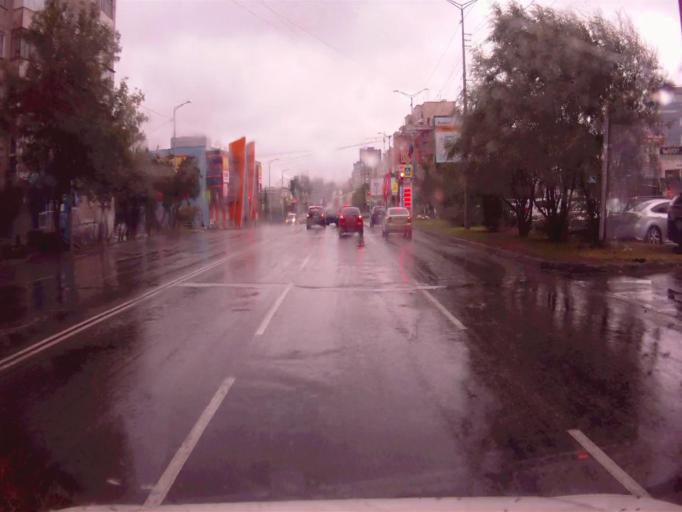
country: RU
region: Chelyabinsk
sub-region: Gorod Chelyabinsk
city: Chelyabinsk
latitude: 55.1625
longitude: 61.4163
